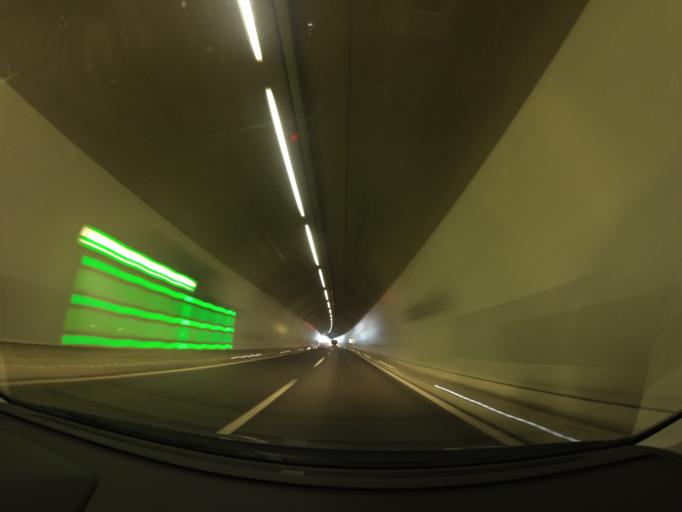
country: CH
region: Saint Gallen
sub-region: Wahlkreis See-Gaster
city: Schmerikon
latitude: 47.2139
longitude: 8.9618
